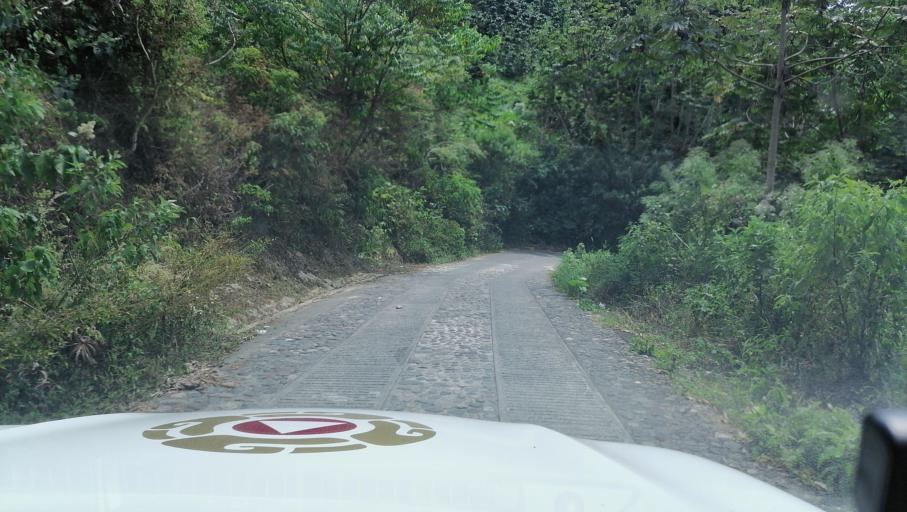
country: MX
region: Chiapas
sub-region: Tapachula
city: Canton Villaflor
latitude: 15.1355
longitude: -92.2890
